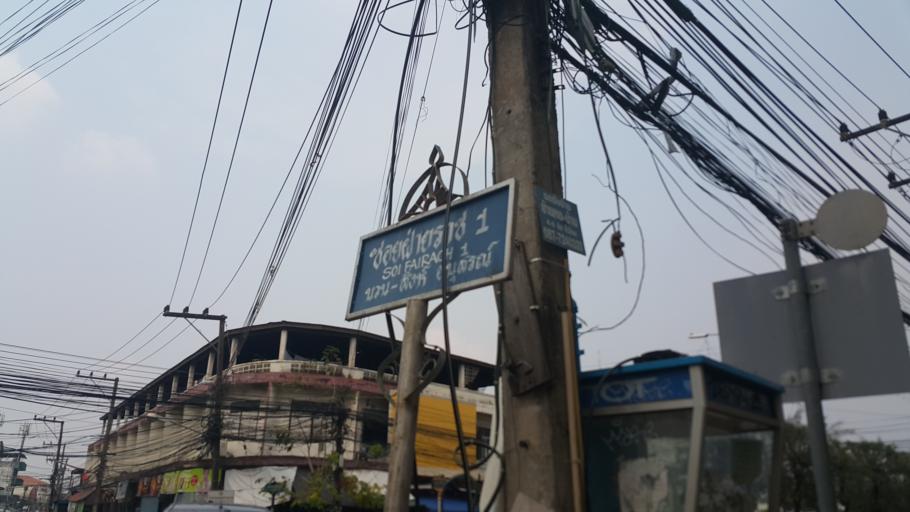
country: TH
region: Changwat Udon Thani
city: Udon Thani
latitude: 17.4041
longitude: 102.8015
